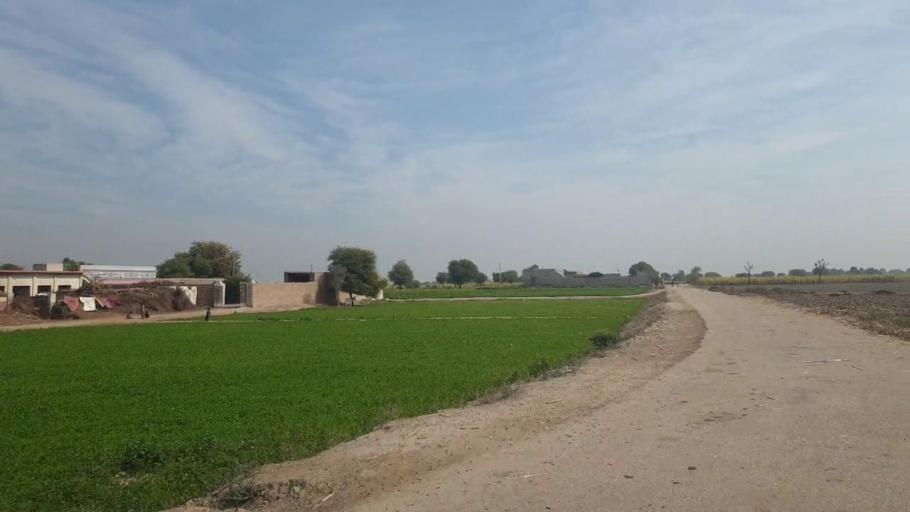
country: PK
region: Sindh
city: Shahpur Chakar
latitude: 26.1357
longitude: 68.5081
